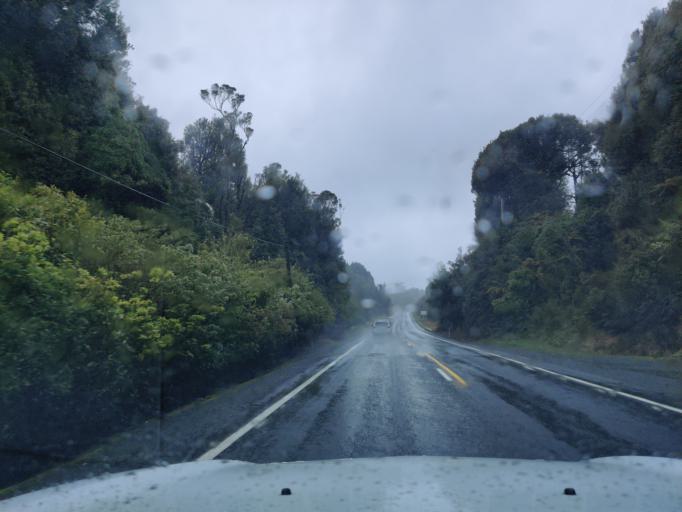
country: NZ
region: Waikato
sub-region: South Waikato District
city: Tokoroa
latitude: -38.0340
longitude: 176.0130
